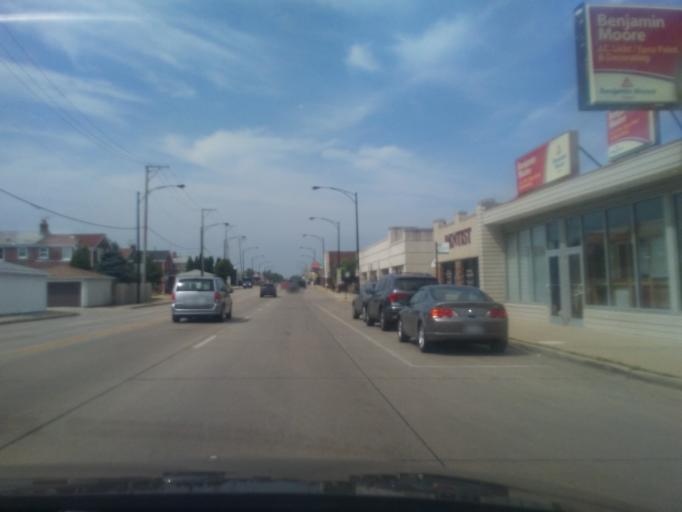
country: US
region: Illinois
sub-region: Cook County
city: Harwood Heights
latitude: 41.9772
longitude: -87.8070
